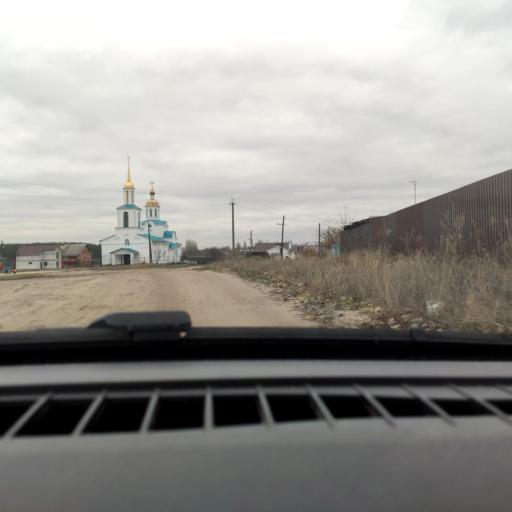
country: RU
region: Voronezj
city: Maslovka
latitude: 51.5804
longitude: 39.3024
